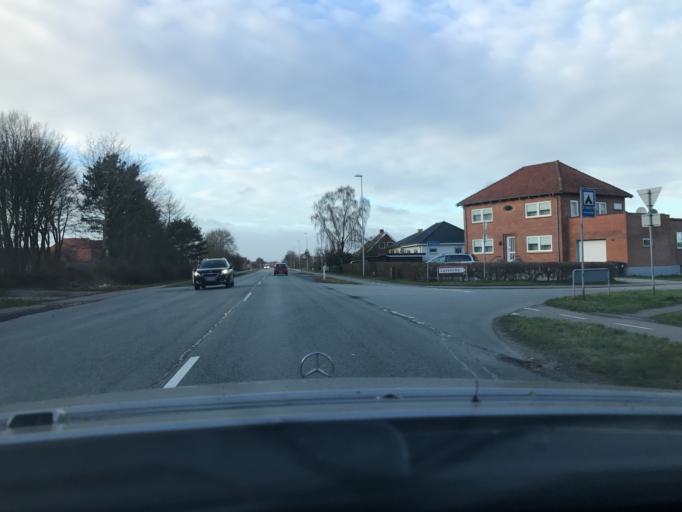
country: DK
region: South Denmark
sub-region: Sonderborg Kommune
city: Nordborg
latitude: 55.0453
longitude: 9.7868
